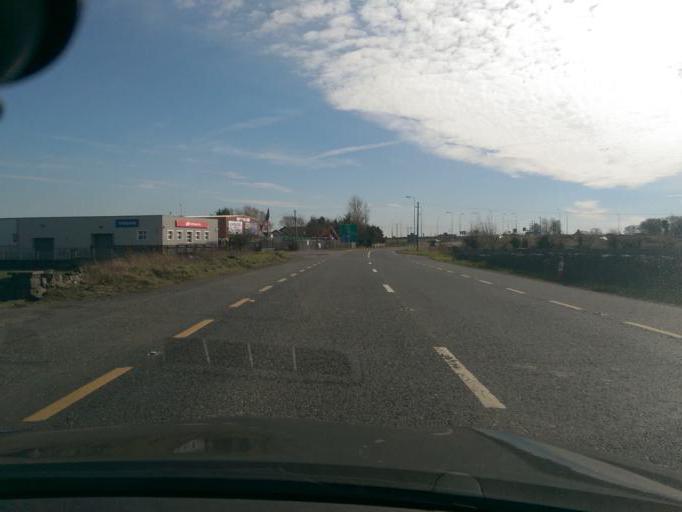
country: IE
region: Connaught
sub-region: County Galway
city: Oranmore
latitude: 53.2987
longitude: -8.9245
